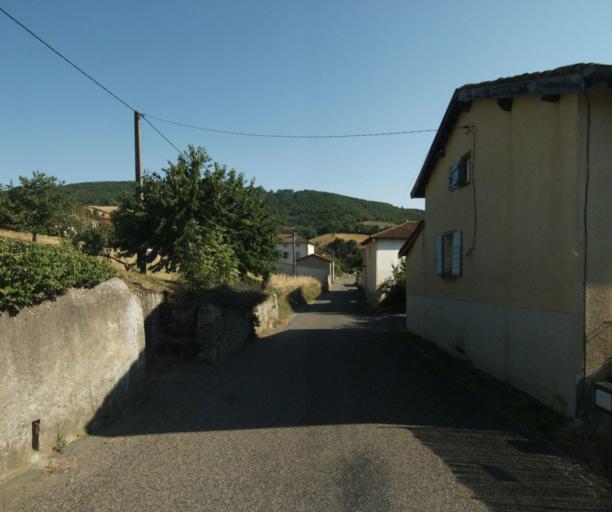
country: FR
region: Rhone-Alpes
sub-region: Departement du Rhone
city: Saint-Pierre-la-Palud
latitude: 45.7839
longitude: 4.6198
